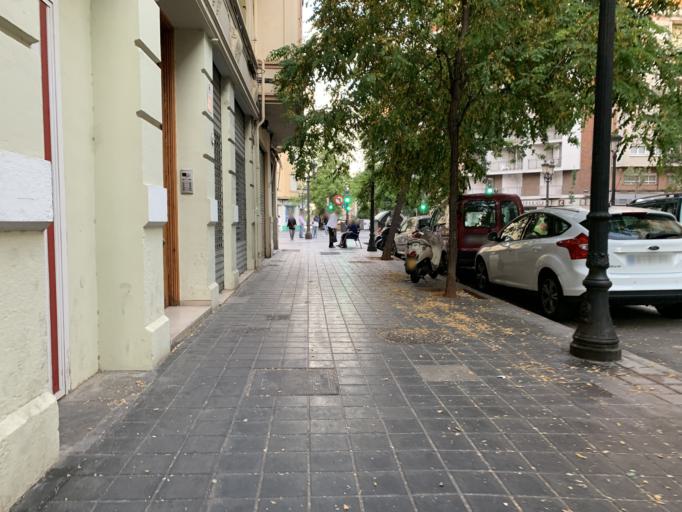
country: ES
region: Valencia
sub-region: Provincia de Valencia
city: Valencia
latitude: 39.4622
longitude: -0.3671
